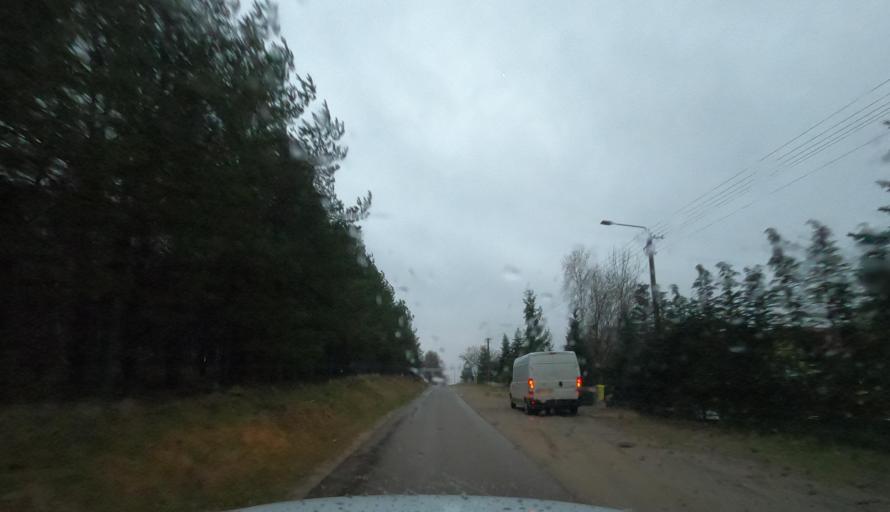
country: PL
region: West Pomeranian Voivodeship
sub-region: Powiat szczecinecki
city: Szczecinek
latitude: 53.7198
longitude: 16.5899
